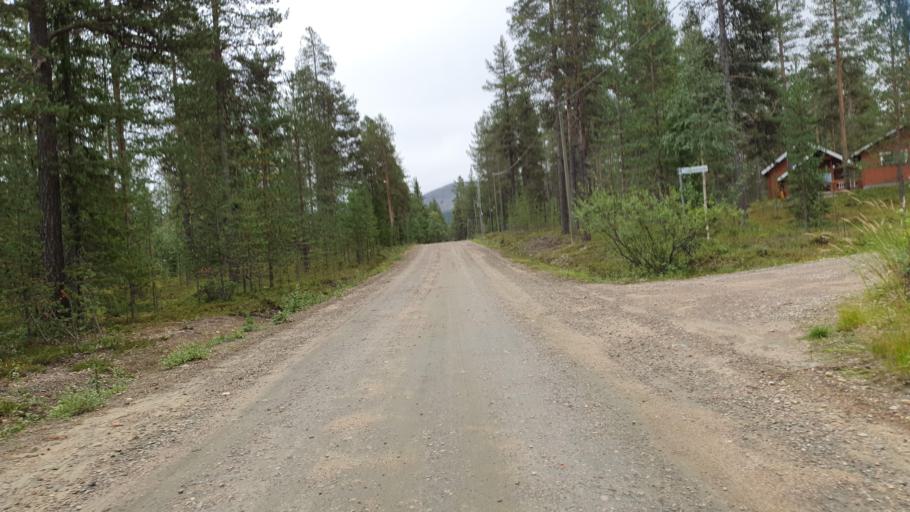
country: FI
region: Lapland
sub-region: Tunturi-Lappi
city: Kolari
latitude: 67.6014
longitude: 24.1884
